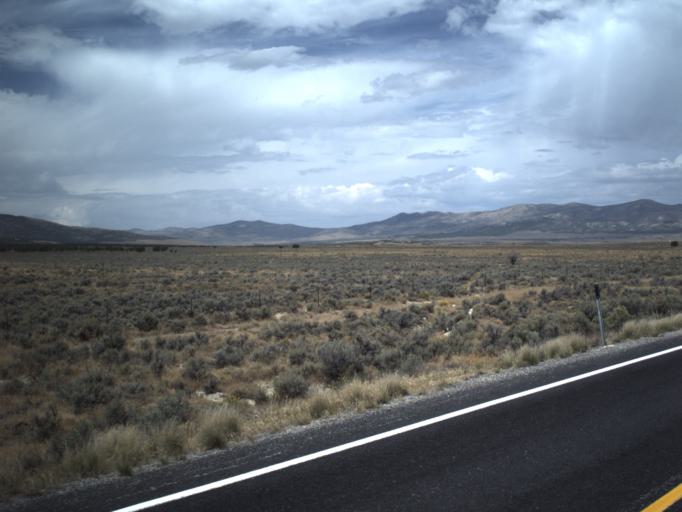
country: US
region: Idaho
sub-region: Cassia County
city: Burley
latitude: 41.7214
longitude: -113.5262
